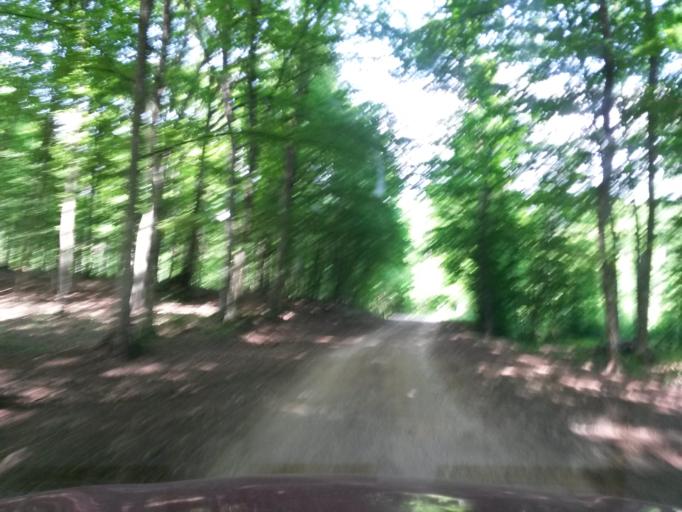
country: SK
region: Kosicky
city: Moldava nad Bodvou
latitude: 48.6442
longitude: 20.9575
